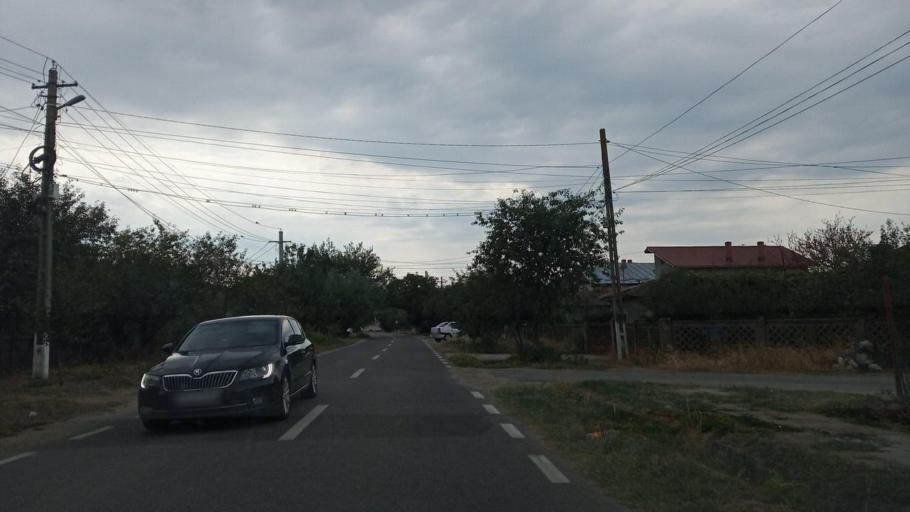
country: RO
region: Giurgiu
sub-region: Comuna Izvoarele
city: Isvoarele
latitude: 44.1694
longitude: 26.3197
